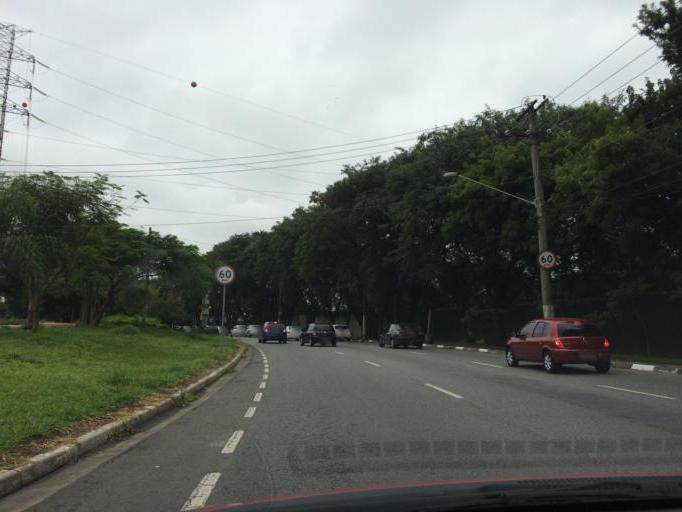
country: BR
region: Sao Paulo
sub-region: Osasco
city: Osasco
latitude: -23.5524
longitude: -46.7326
